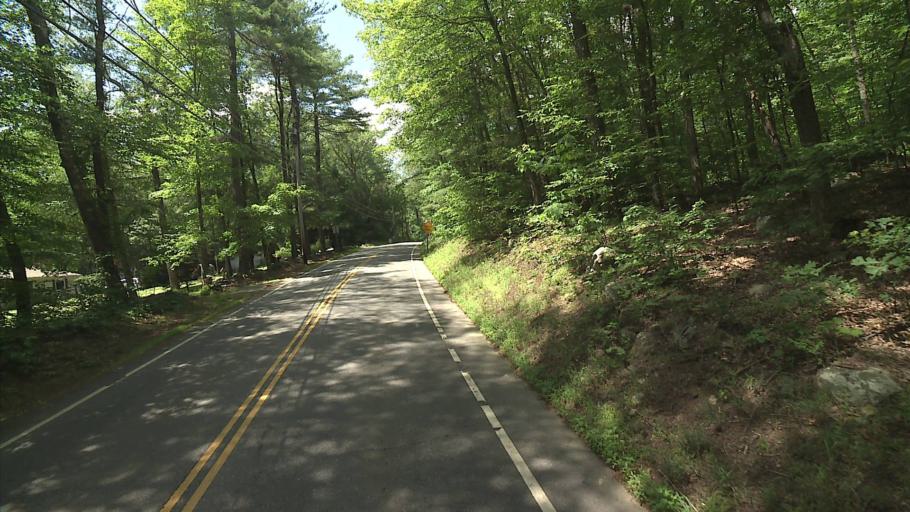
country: US
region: Massachusetts
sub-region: Worcester County
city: Southbridge
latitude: 41.9749
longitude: -72.0704
